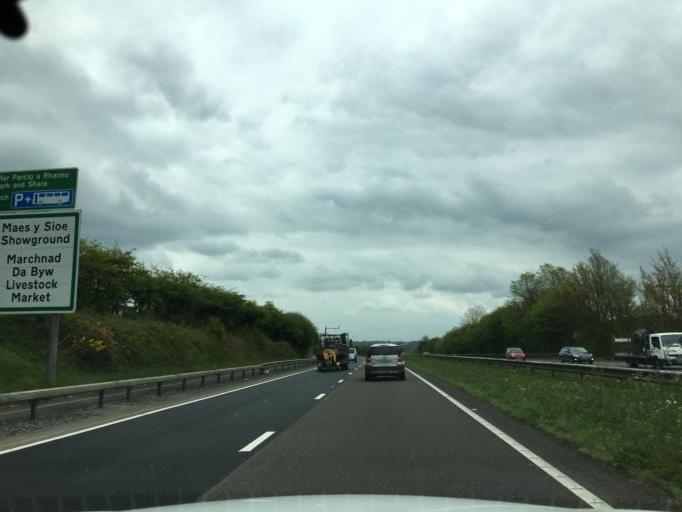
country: GB
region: Wales
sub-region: Carmarthenshire
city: Llangain
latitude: 51.8475
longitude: -4.3522
